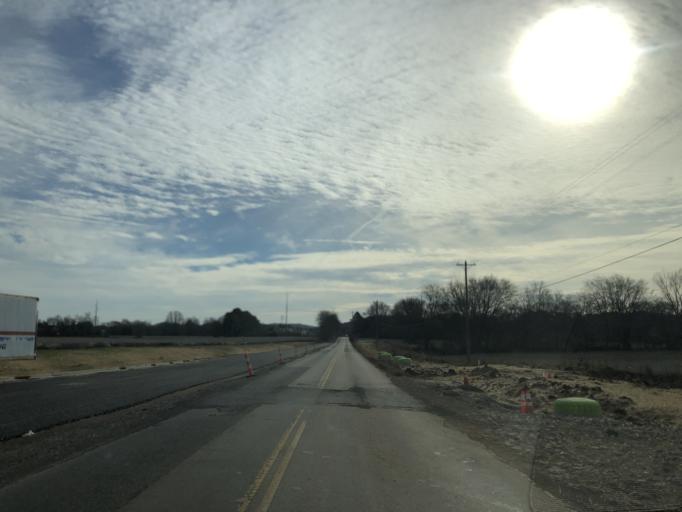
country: US
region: Tennessee
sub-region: Williamson County
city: Franklin
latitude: 35.9423
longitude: -86.9030
